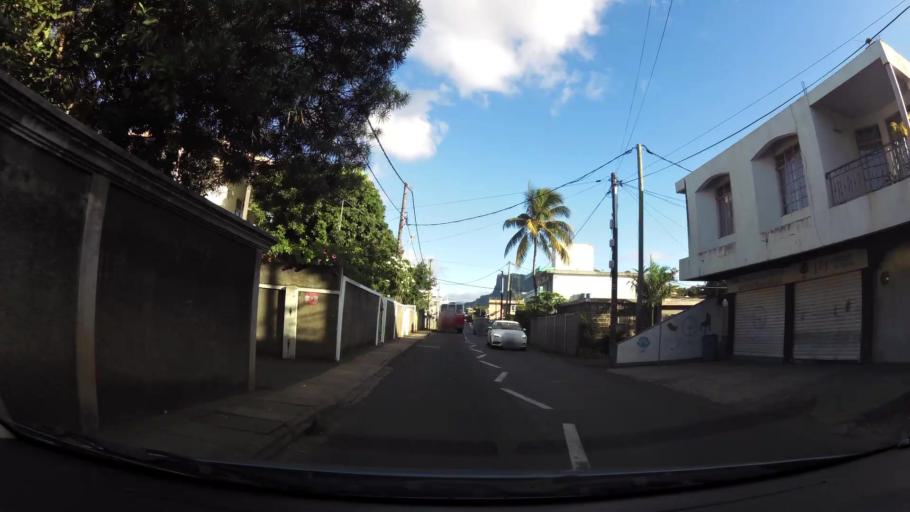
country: MU
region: Plaines Wilhems
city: Ebene
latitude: -20.2312
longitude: 57.4632
